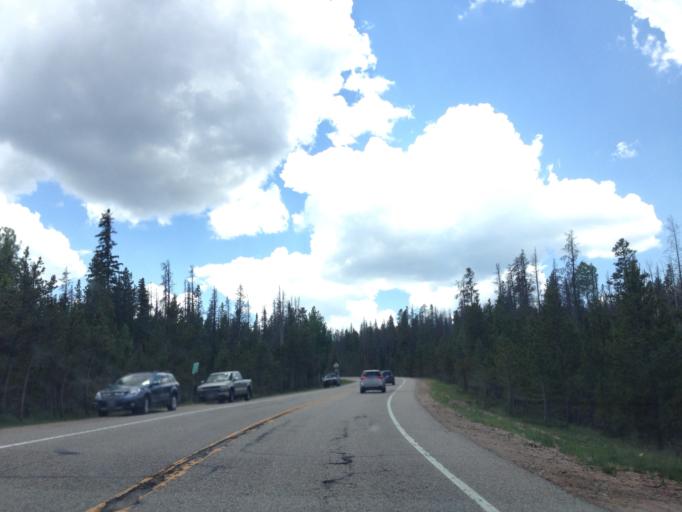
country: US
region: Colorado
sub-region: Larimer County
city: Estes Park
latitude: 40.5992
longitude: -105.8390
